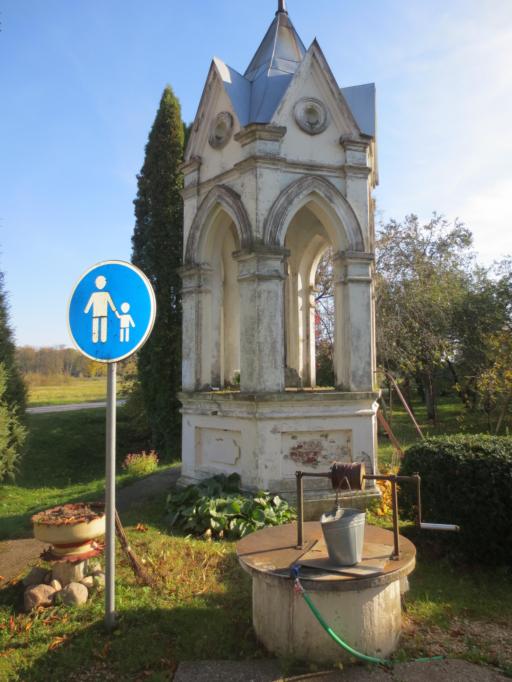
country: LT
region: Utenos apskritis
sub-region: Anyksciai
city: Anyksciai
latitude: 55.4681
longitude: 24.8822
